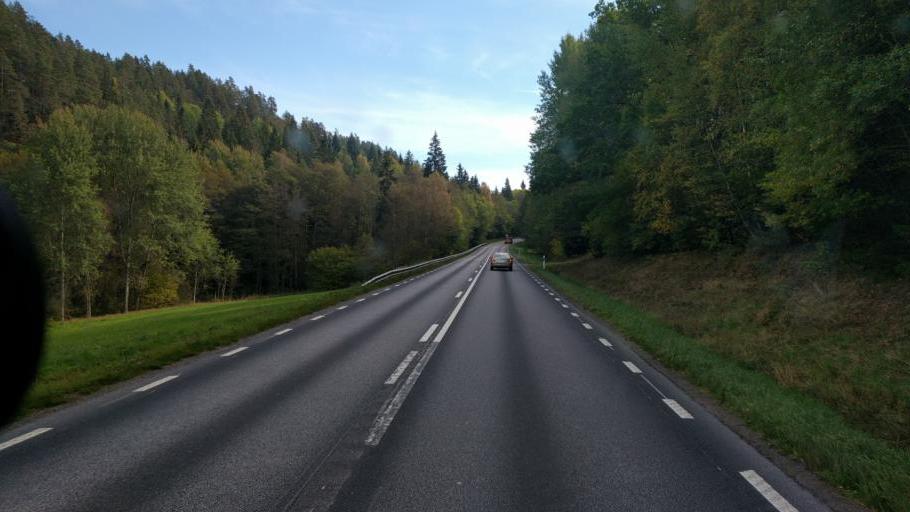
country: SE
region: OEstergoetland
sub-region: Kinda Kommun
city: Kisa
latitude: 57.9712
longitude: 15.6489
